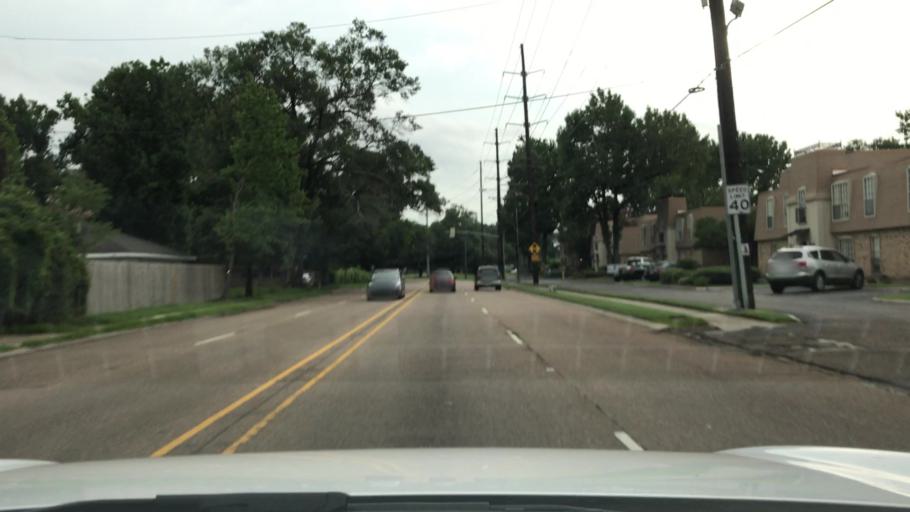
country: US
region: Louisiana
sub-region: East Baton Rouge Parish
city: Baton Rouge
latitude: 30.4284
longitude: -91.1362
